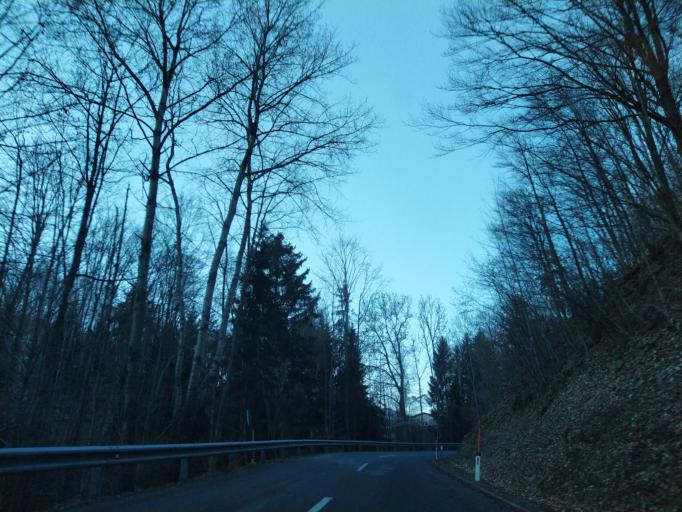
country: AT
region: Upper Austria
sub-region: Politischer Bezirk Urfahr-Umgebung
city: Kirchschlag bei Linz
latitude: 48.3908
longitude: 14.2878
